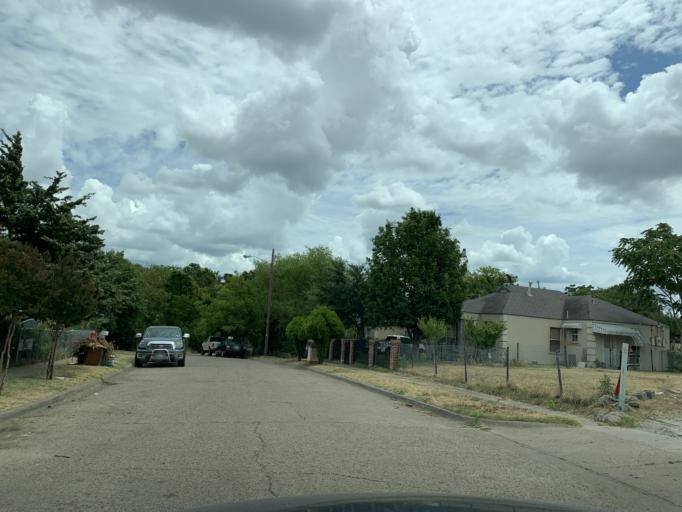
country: US
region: Texas
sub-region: Dallas County
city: Cockrell Hill
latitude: 32.7461
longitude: -96.8792
